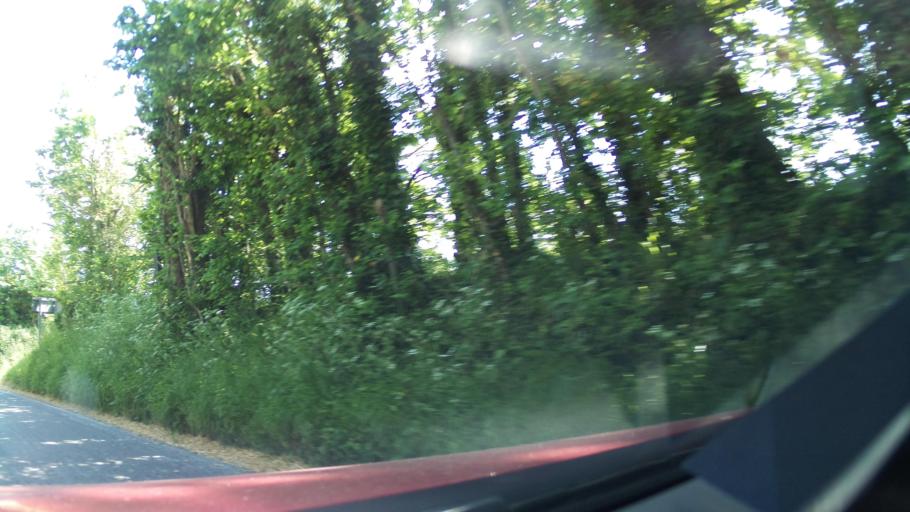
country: GB
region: England
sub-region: Wiltshire
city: Rushall
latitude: 51.2694
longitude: -1.8030
